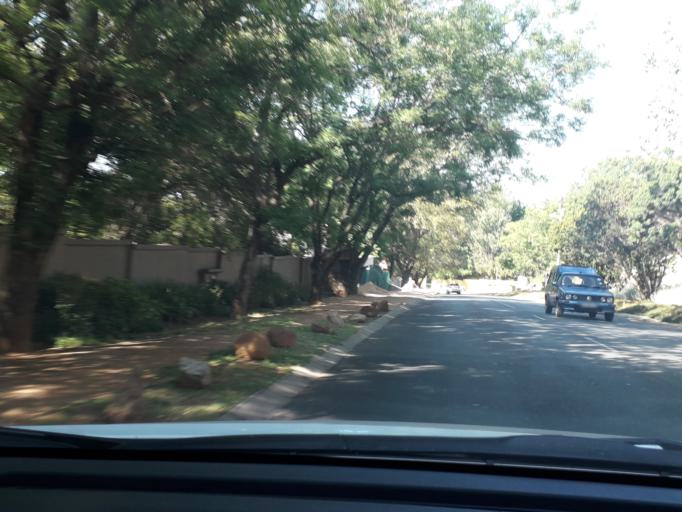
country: ZA
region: Gauteng
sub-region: City of Johannesburg Metropolitan Municipality
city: Midrand
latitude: -26.0678
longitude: 28.0340
